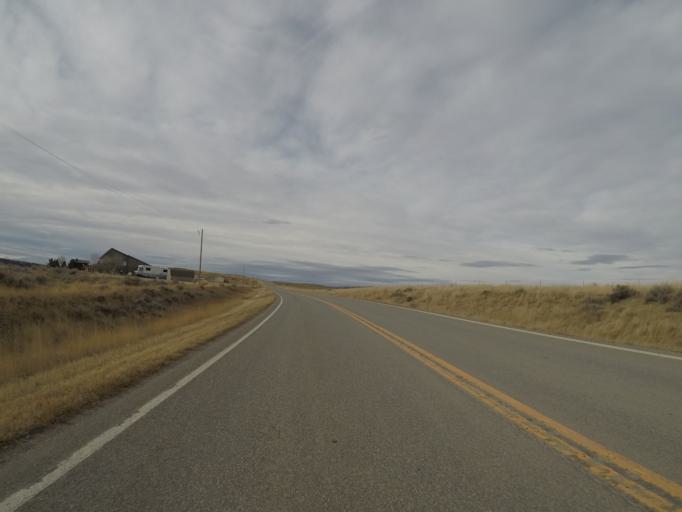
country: US
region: Montana
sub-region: Yellowstone County
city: Laurel
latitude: 45.8421
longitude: -108.7232
